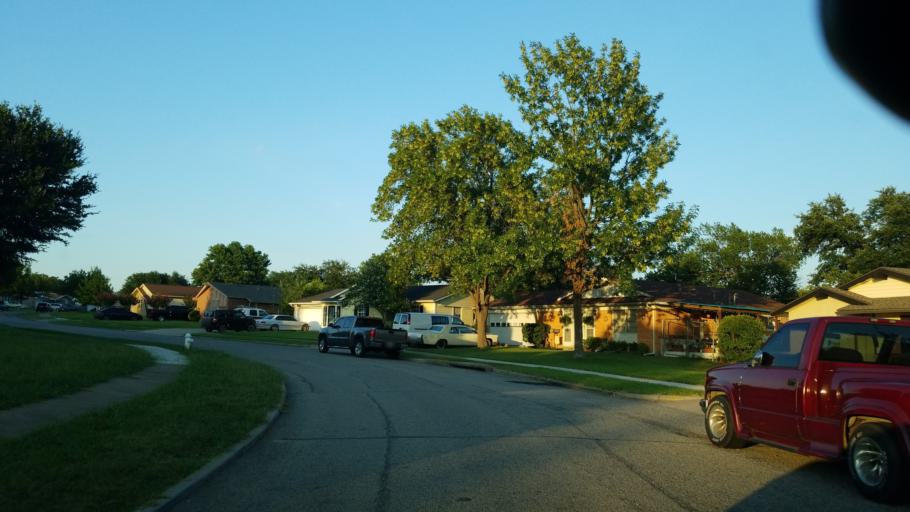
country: US
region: Texas
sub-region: Dallas County
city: Carrollton
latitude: 32.9413
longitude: -96.8820
